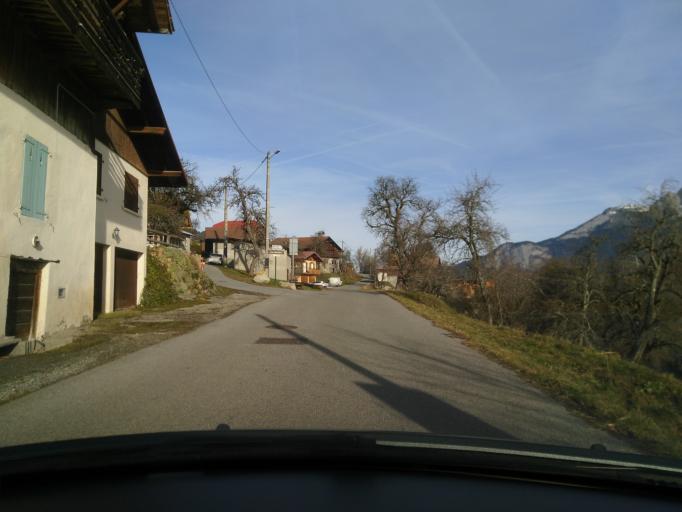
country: FR
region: Rhone-Alpes
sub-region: Departement de la Haute-Savoie
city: Sallanches
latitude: 45.9501
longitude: 6.6178
